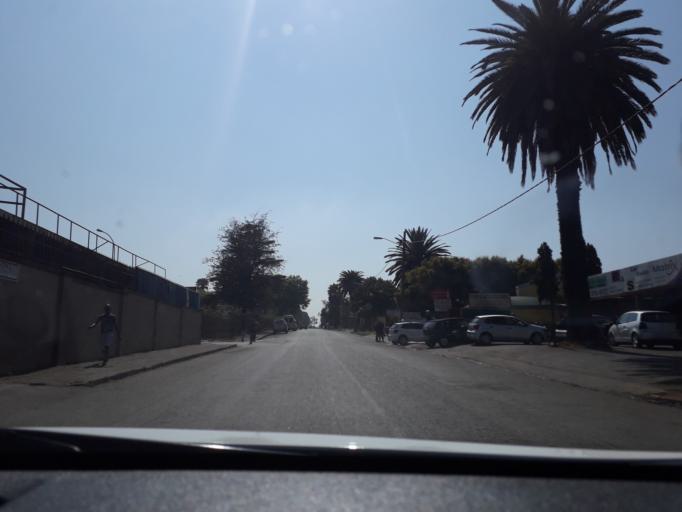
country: ZA
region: Gauteng
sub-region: City of Johannesburg Metropolitan Municipality
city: Modderfontein
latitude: -26.1108
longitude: 28.2318
